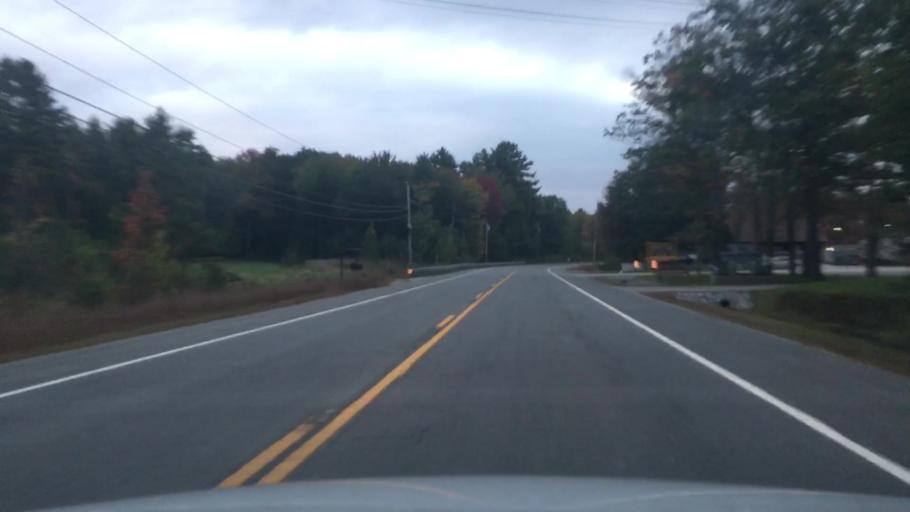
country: US
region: Maine
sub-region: York County
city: Buxton
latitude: 43.6446
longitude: -70.4904
